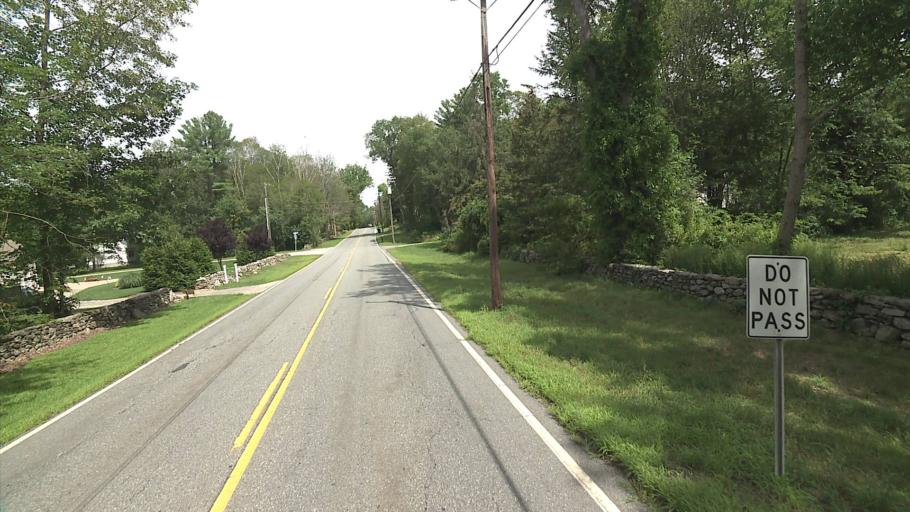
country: US
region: Connecticut
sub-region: Windham County
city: Putnam
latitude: 41.8969
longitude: -71.8666
